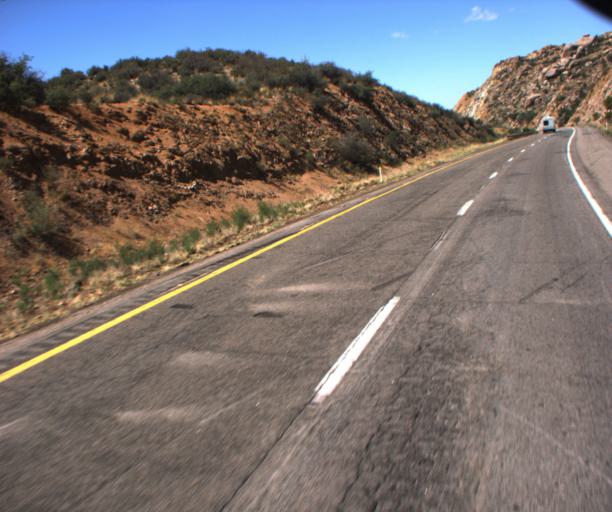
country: US
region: Arizona
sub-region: Mohave County
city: Peach Springs
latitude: 35.1744
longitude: -113.5032
